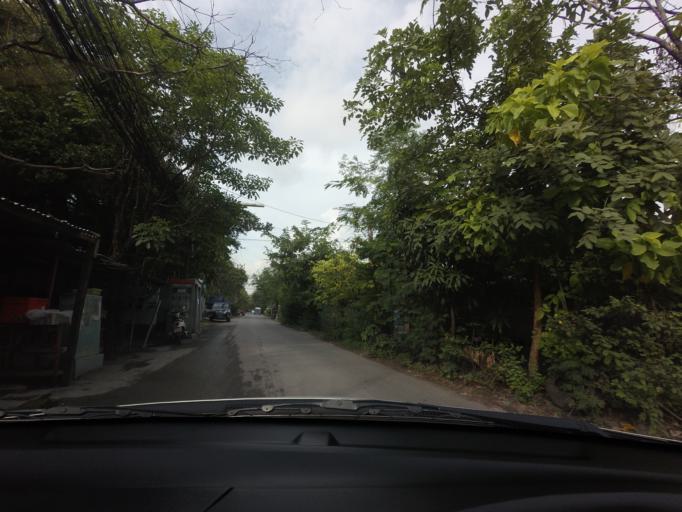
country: TH
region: Bangkok
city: Chatuchak
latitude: 13.8214
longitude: 100.5544
